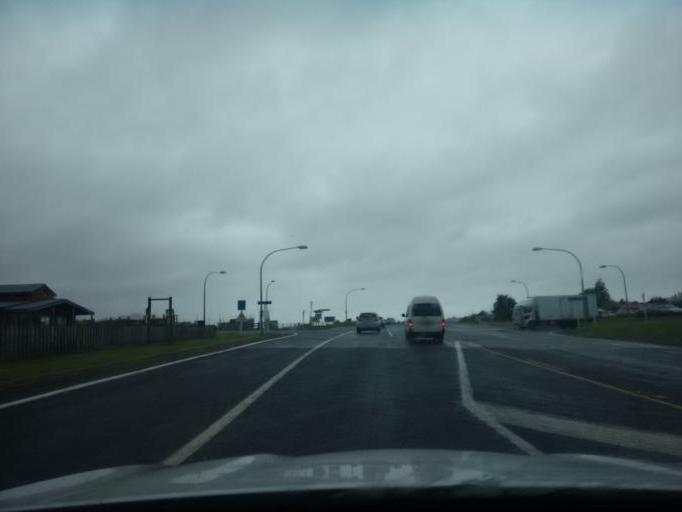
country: NZ
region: Waikato
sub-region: Thames-Coromandel District
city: Whitianga
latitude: -36.8335
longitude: 175.6737
